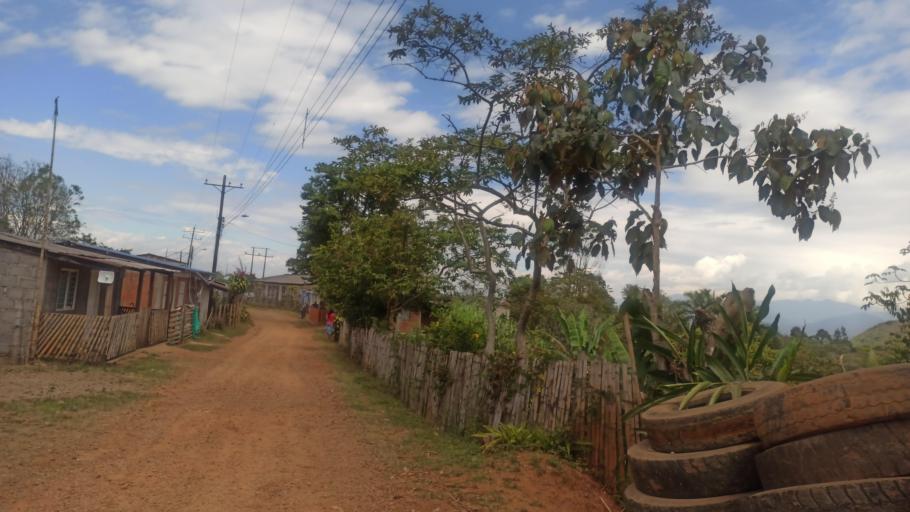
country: CO
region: Valle del Cauca
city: Jamundi
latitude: 3.2080
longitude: -76.6532
